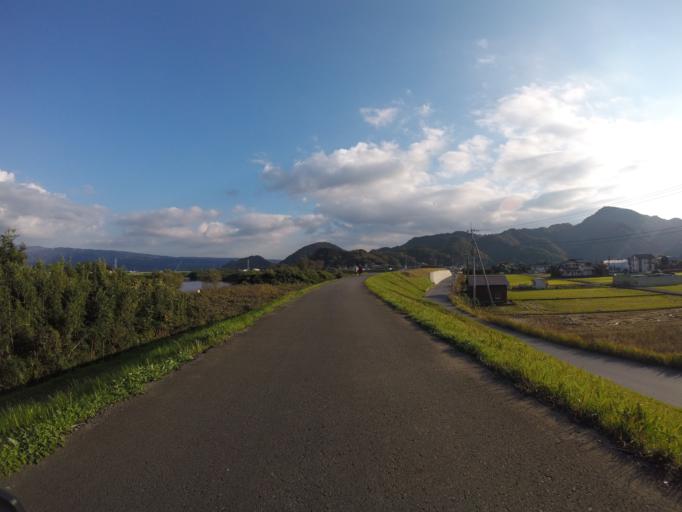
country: JP
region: Shizuoka
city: Mishima
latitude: 35.0780
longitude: 138.9127
